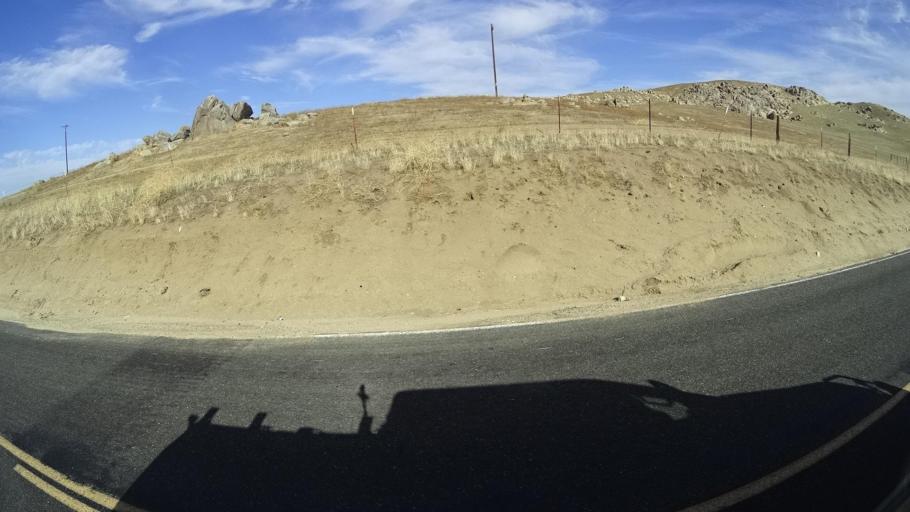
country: US
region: California
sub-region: Kern County
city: Oildale
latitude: 35.6120
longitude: -118.8742
